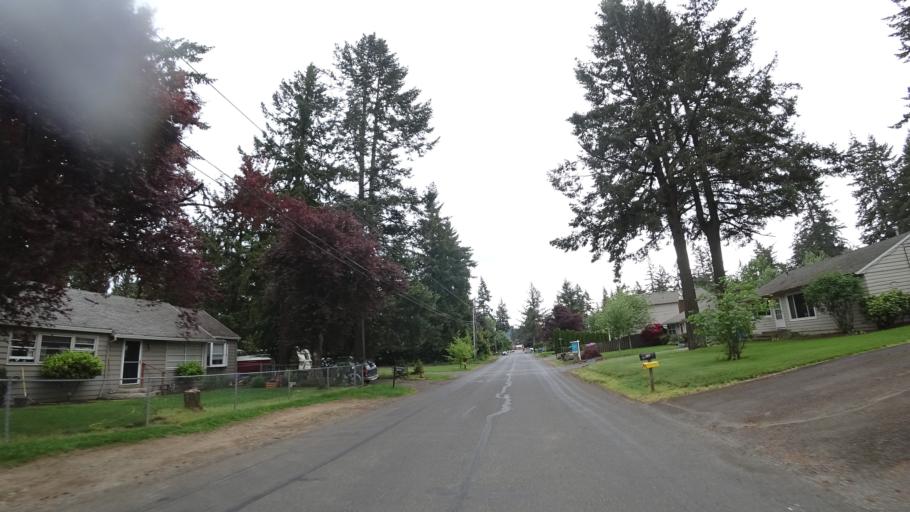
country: US
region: Oregon
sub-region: Multnomah County
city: Lents
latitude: 45.5074
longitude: -122.5173
